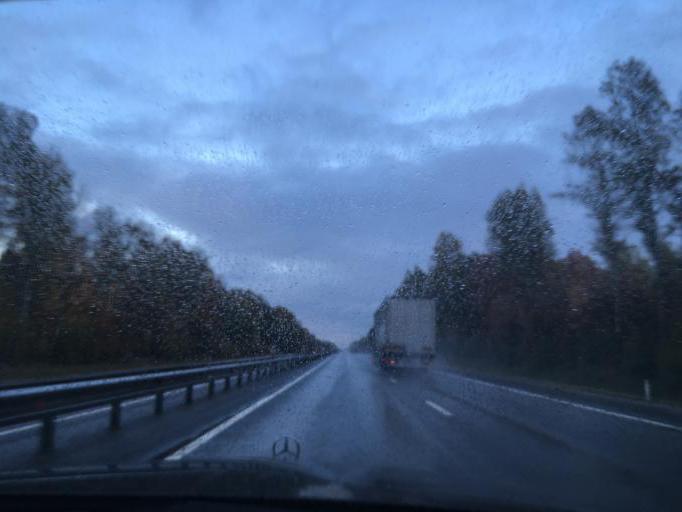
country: RU
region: Smolensk
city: Yartsevo
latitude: 55.0890
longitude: 32.8154
